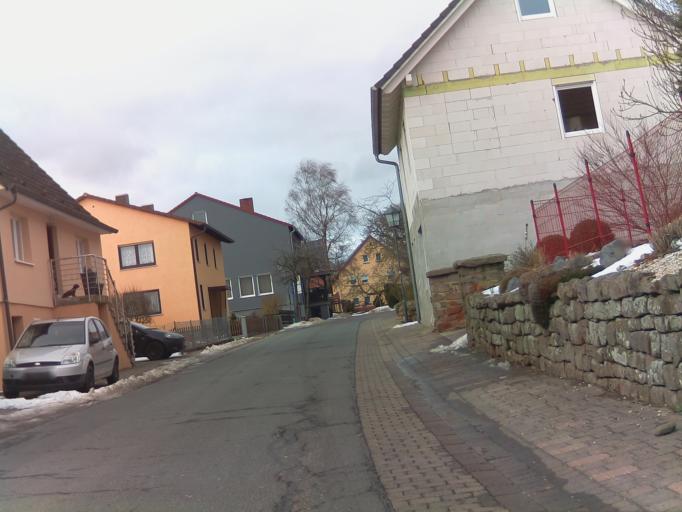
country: DE
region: Hesse
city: Michelstadt
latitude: 49.6563
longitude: 9.0687
